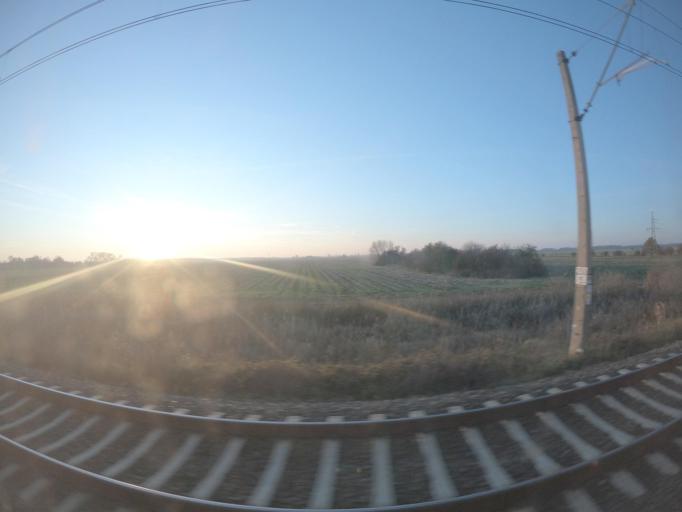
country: PL
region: Lubusz
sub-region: Powiat gorzowski
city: Kostrzyn nad Odra
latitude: 52.5473
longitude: 14.6510
